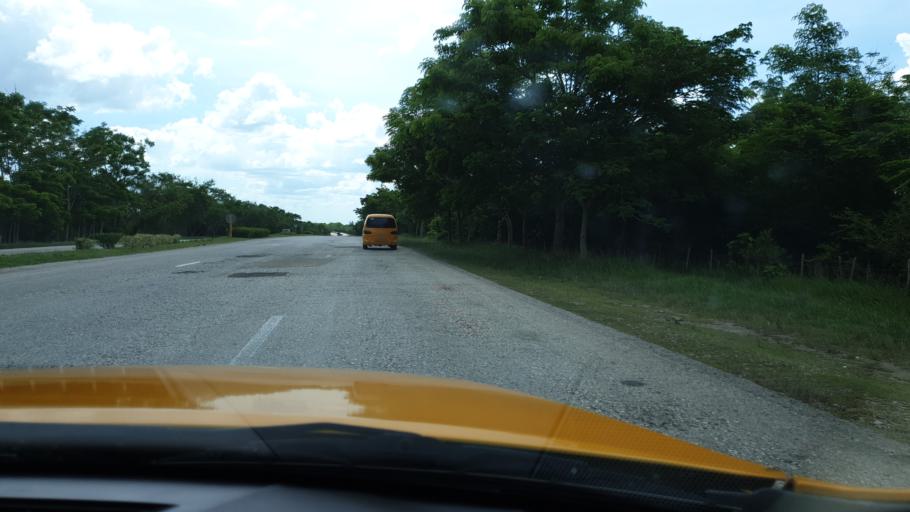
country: CU
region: Cienfuegos
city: Cruces
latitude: 22.4535
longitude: -80.2938
